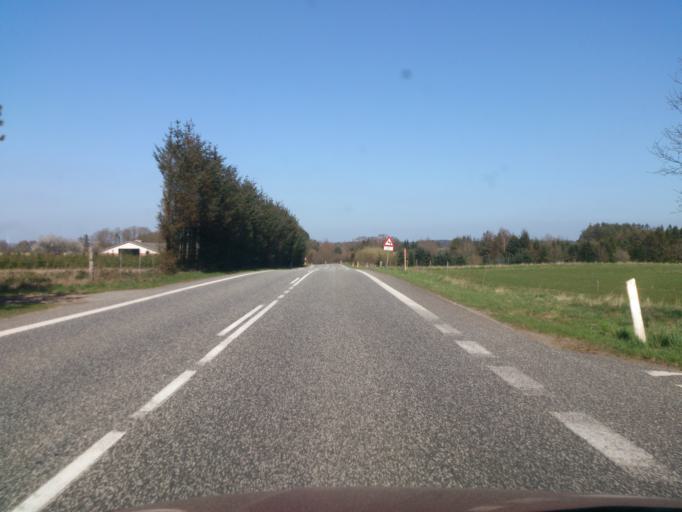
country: DK
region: Central Jutland
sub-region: Viborg Kommune
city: Bjerringbro
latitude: 56.4452
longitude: 9.7128
